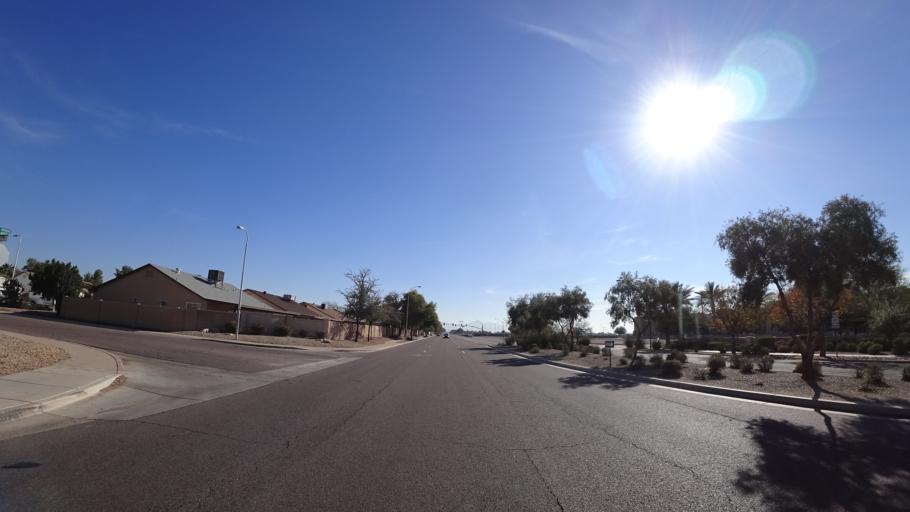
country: US
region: Arizona
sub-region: Maricopa County
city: Peoria
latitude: 33.5322
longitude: -112.2550
